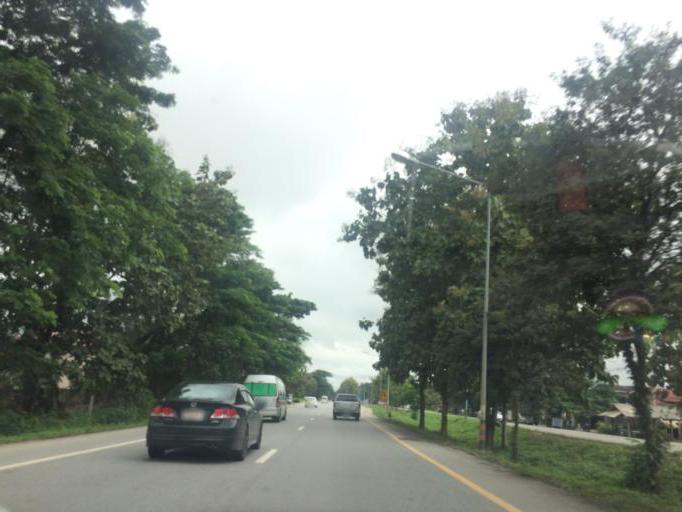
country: TH
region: Chiang Rai
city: Mae Lao
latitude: 19.8285
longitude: 99.7771
